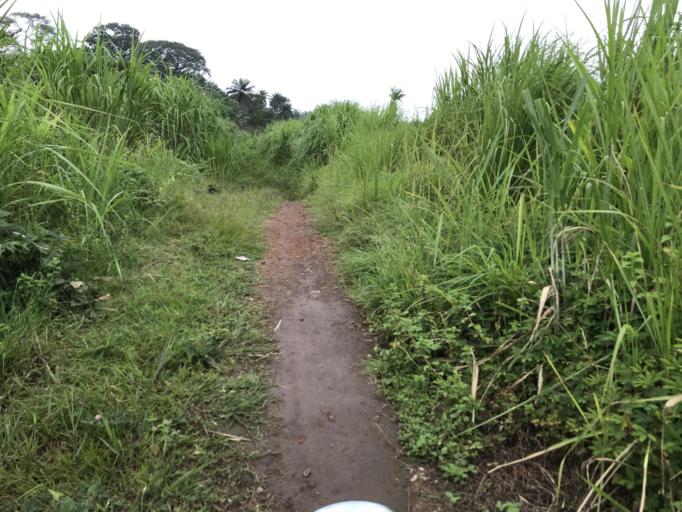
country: GN
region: Nzerekore
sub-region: Prefecture de Guekedou
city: Gueckedou
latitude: 8.4720
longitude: -10.3079
